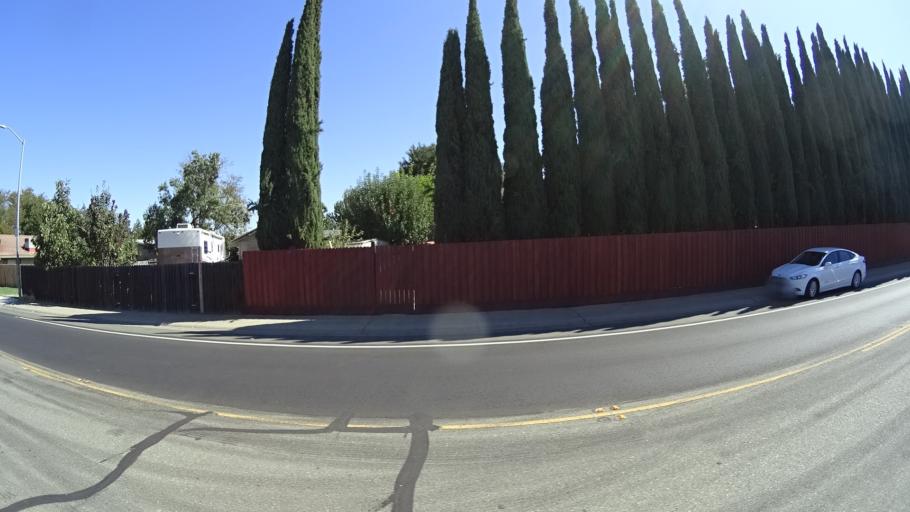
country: US
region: California
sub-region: Sacramento County
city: Elk Grove
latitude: 38.3999
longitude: -121.3715
